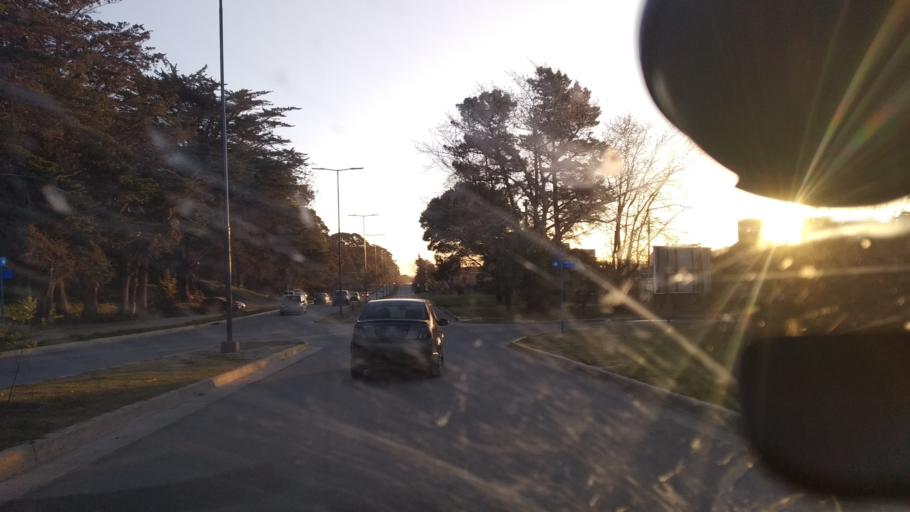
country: AR
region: Buenos Aires
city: Necochea
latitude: -38.5841
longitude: -58.7469
